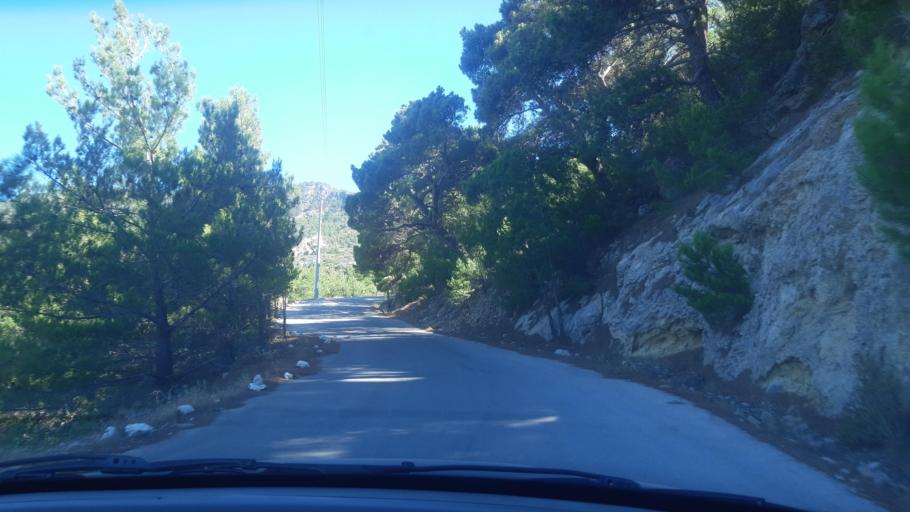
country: GR
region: South Aegean
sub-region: Nomos Dodekanisou
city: Karpathos
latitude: 35.5809
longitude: 27.1791
